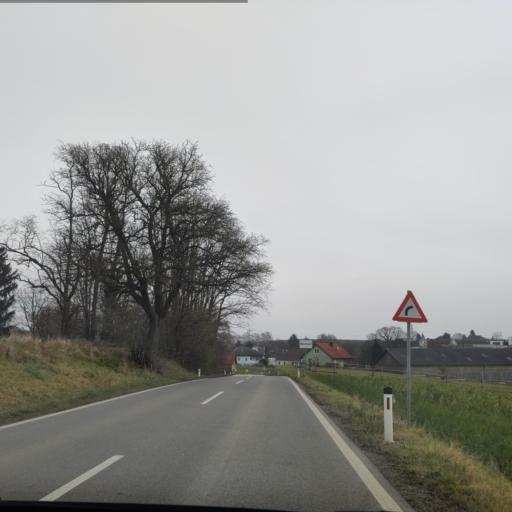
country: AT
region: Lower Austria
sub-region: Politischer Bezirk Sankt Polten
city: Karlstetten
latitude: 48.2218
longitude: 15.5882
